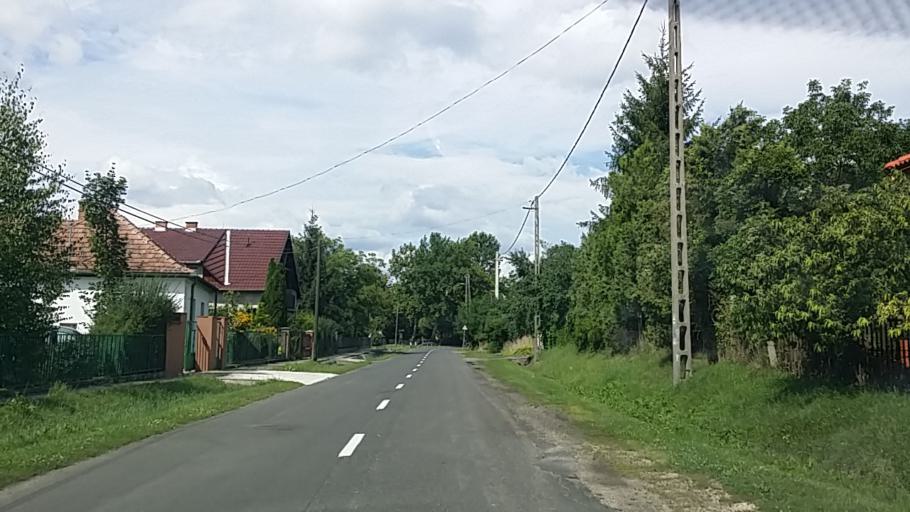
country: SK
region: Nitriansky
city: Sahy
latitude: 48.0497
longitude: 18.9894
